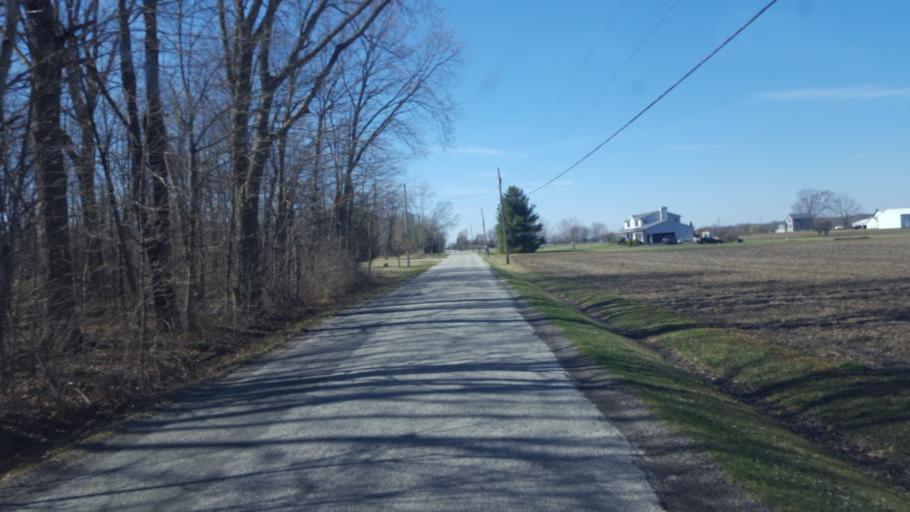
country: US
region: Ohio
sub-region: Marion County
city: Marion
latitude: 40.4986
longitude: -83.1013
